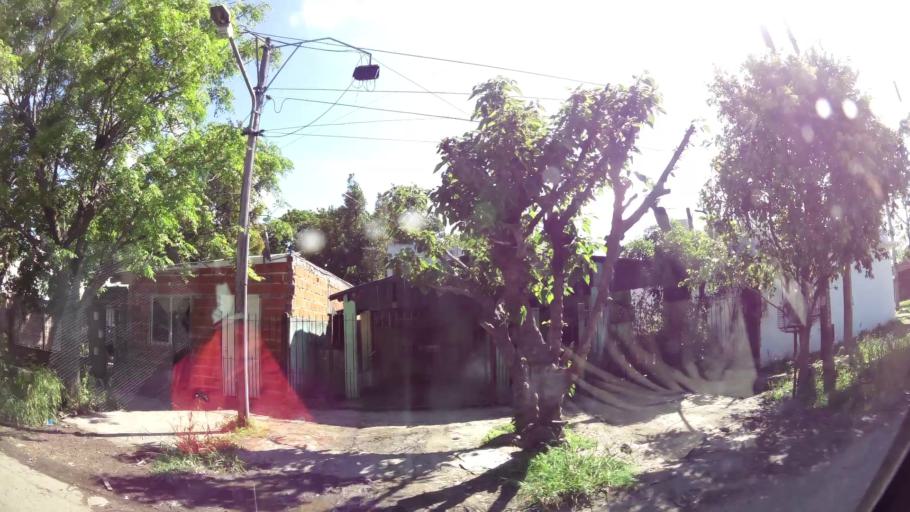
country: AR
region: Buenos Aires
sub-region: Partido de Quilmes
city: Quilmes
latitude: -34.8001
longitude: -58.2468
